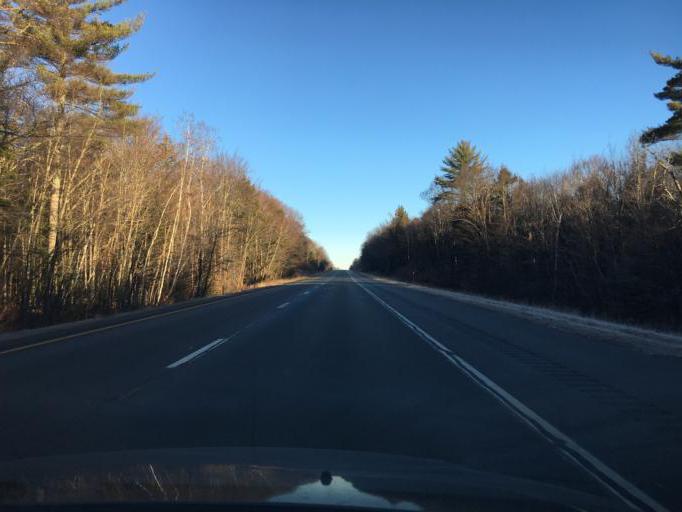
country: US
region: New Hampshire
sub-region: Belknap County
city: Sanbornton
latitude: 43.5399
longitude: -71.6146
